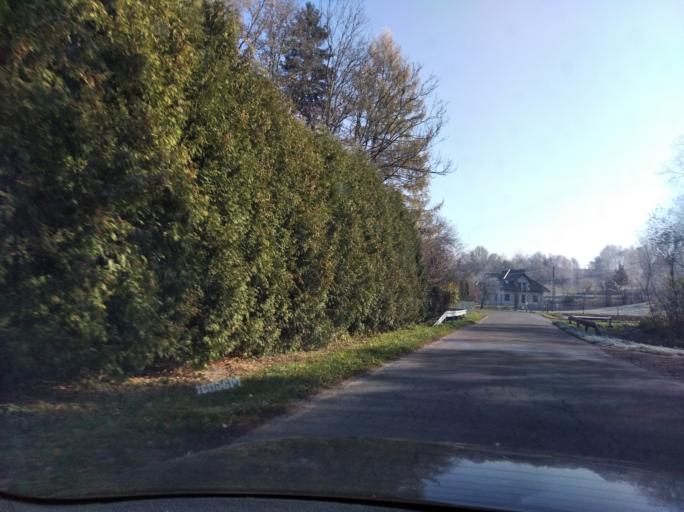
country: PL
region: Subcarpathian Voivodeship
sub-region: Powiat strzyzowski
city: Wysoka Strzyzowska
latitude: 49.8347
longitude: 21.7255
